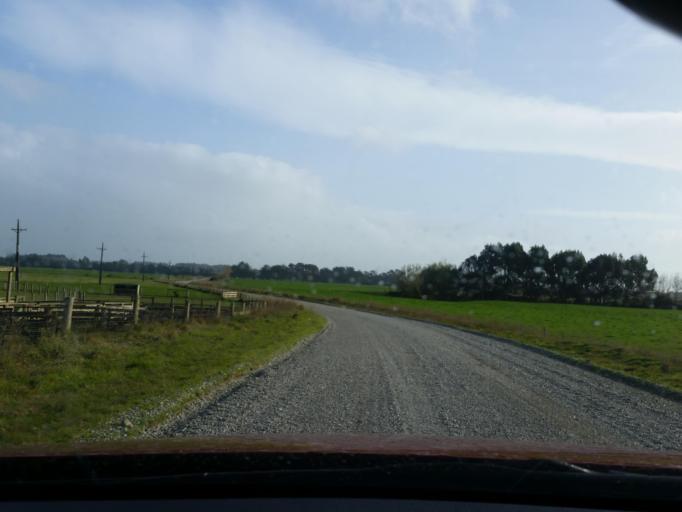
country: NZ
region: Southland
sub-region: Invercargill City
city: Invercargill
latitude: -46.2914
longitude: 168.4306
